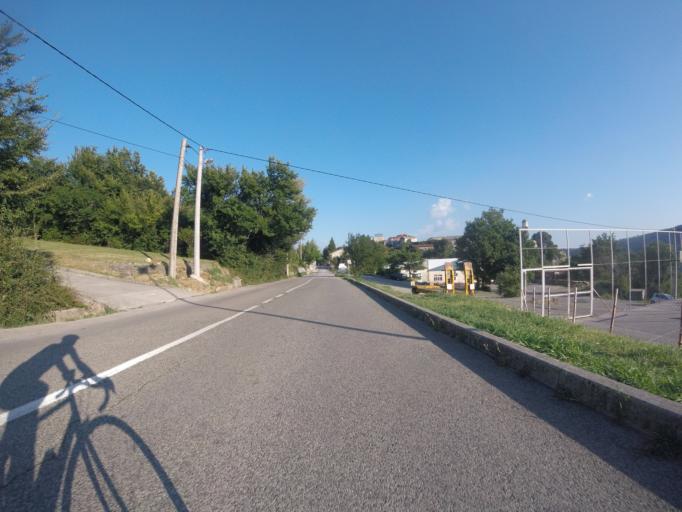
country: HR
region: Primorsko-Goranska
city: Bribir
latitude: 45.1640
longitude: 14.7584
